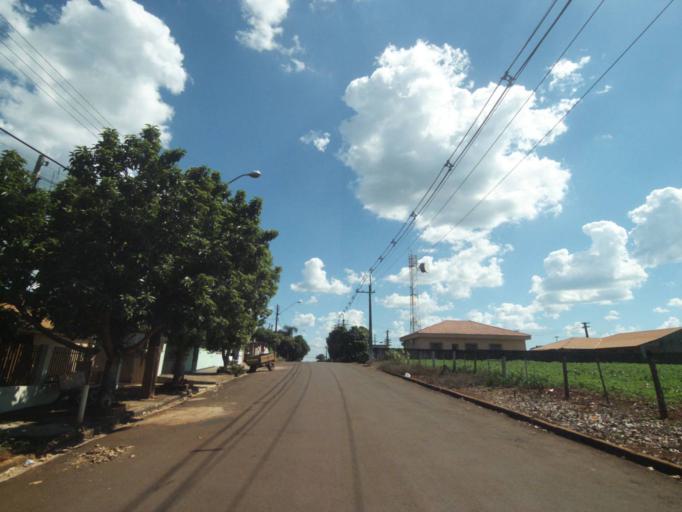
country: BR
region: Parana
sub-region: Sertanopolis
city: Sertanopolis
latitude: -23.0430
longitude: -50.8220
